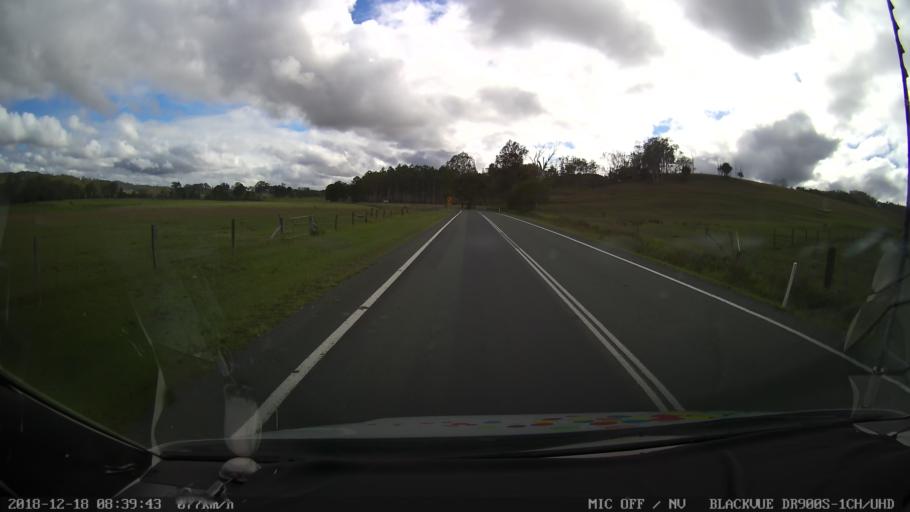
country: AU
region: Queensland
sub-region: Logan
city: Cedar Vale
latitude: -28.2486
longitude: 152.8413
